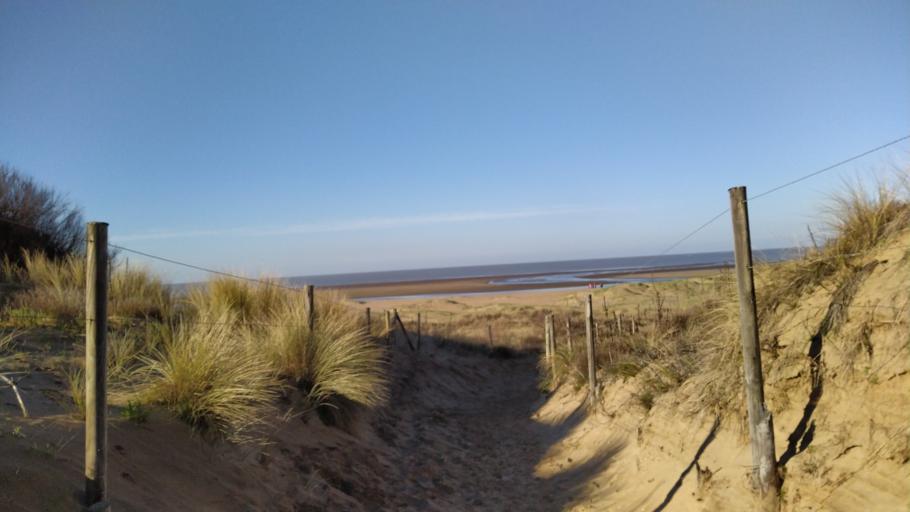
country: FR
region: Pays de la Loire
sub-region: Departement de la Loire-Atlantique
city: Saint-Michel-Chef-Chef
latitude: 47.2138
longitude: -2.1621
